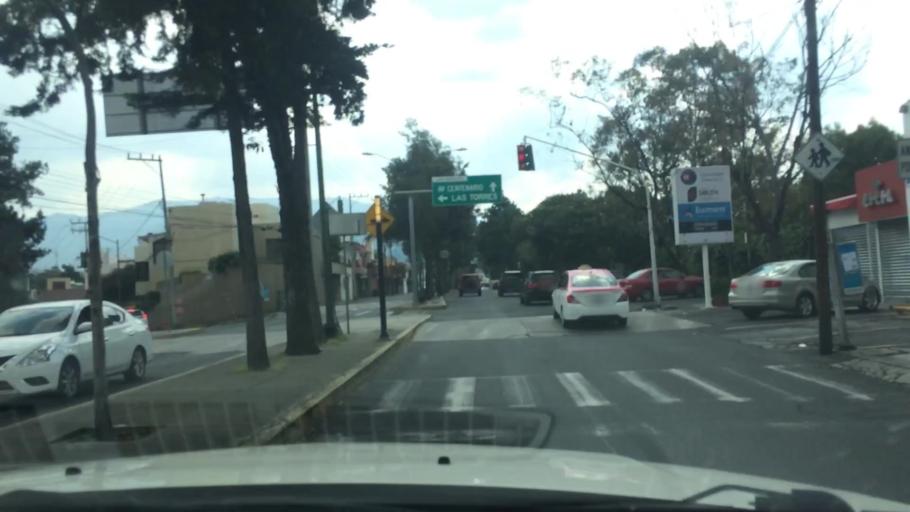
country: MX
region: Mexico City
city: Magdalena Contreras
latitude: 19.3440
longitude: -99.2413
